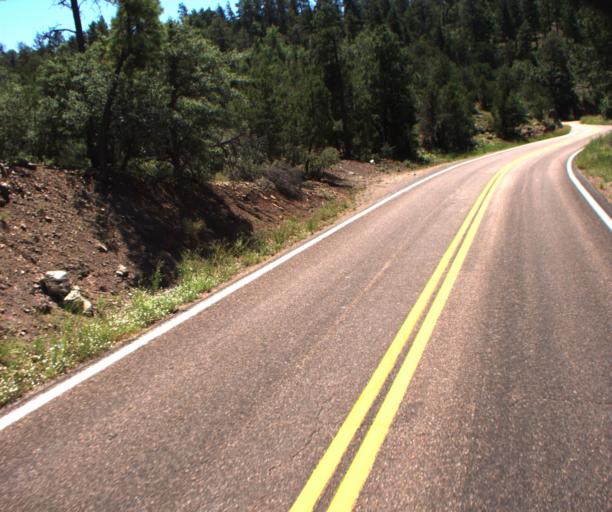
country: US
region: Arizona
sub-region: Greenlee County
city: Morenci
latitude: 33.2092
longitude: -109.3758
